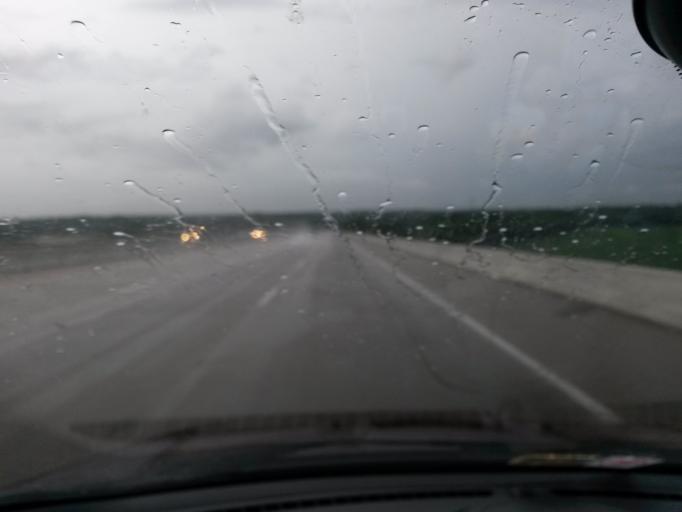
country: US
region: Virginia
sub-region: Chesterfield County
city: Enon
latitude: 37.3829
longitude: -77.3464
